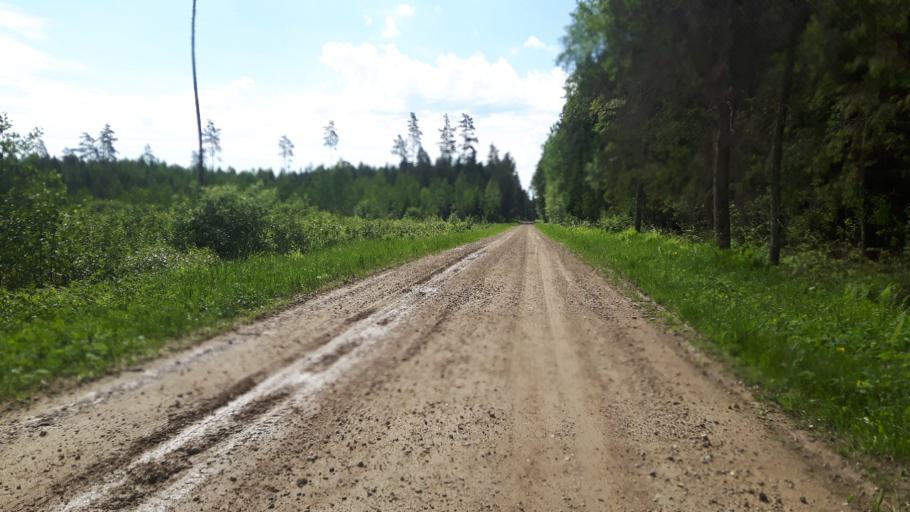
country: EE
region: Paernumaa
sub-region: Vaendra vald (alev)
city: Vandra
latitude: 58.7288
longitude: 25.0305
